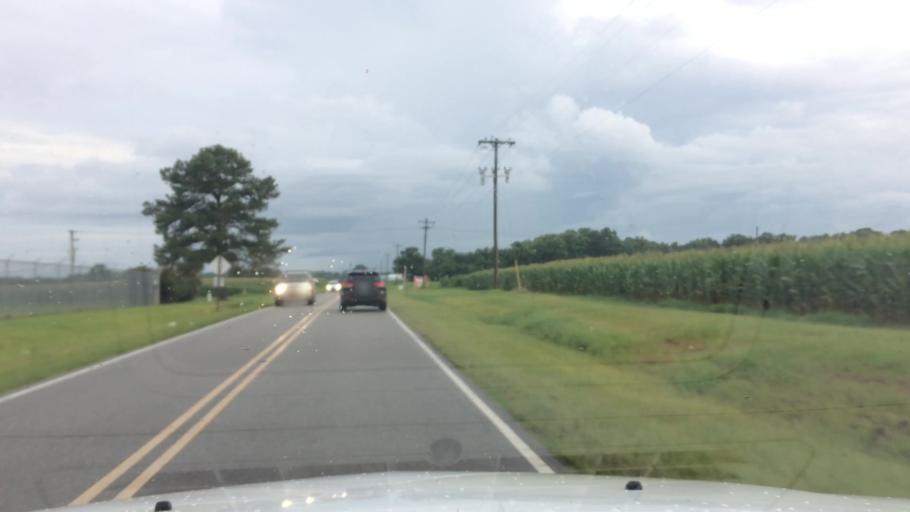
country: US
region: North Carolina
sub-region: Pitt County
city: Farmville
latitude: 35.5781
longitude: -77.5519
